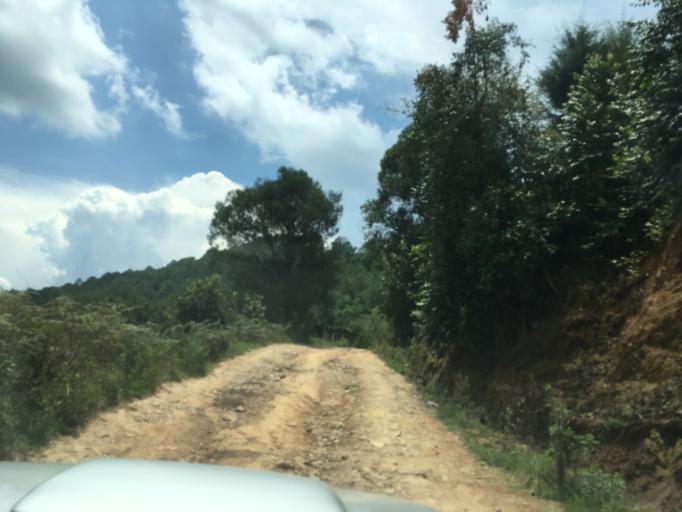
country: MX
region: Michoacan
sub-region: Zitacuaro
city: Macutzio
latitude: 19.5020
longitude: -100.3316
